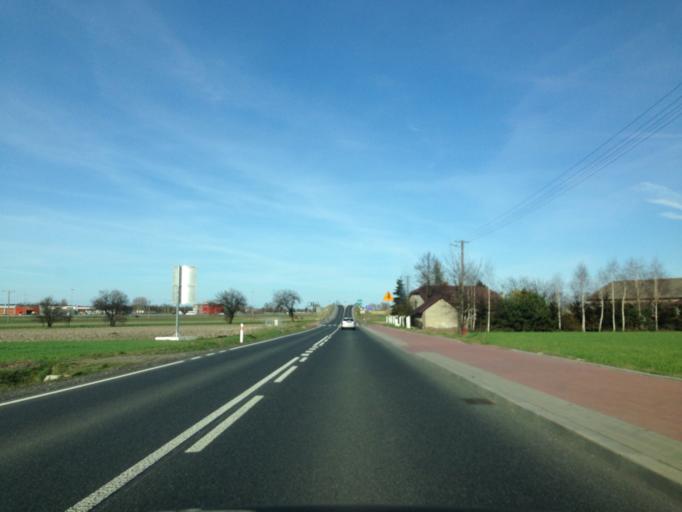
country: PL
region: Lodz Voivodeship
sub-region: Powiat poddebicki
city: Wartkowice
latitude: 51.9908
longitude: 19.0400
